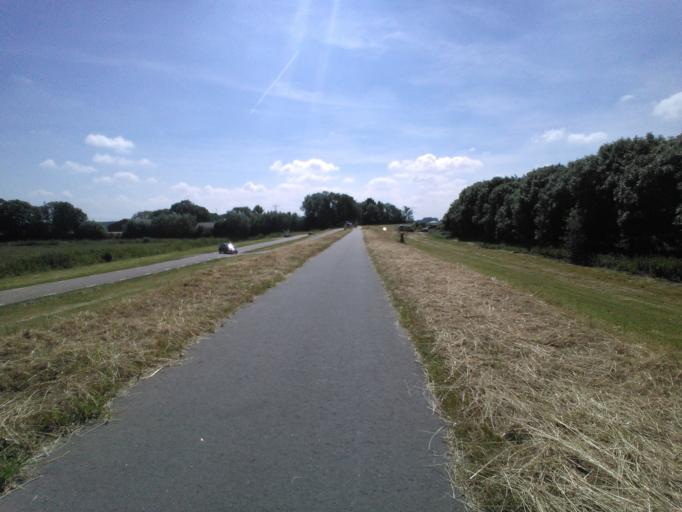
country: NL
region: North Brabant
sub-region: Gemeente Geertruidenberg
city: Geertruidenberg
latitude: 51.7458
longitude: 4.8538
